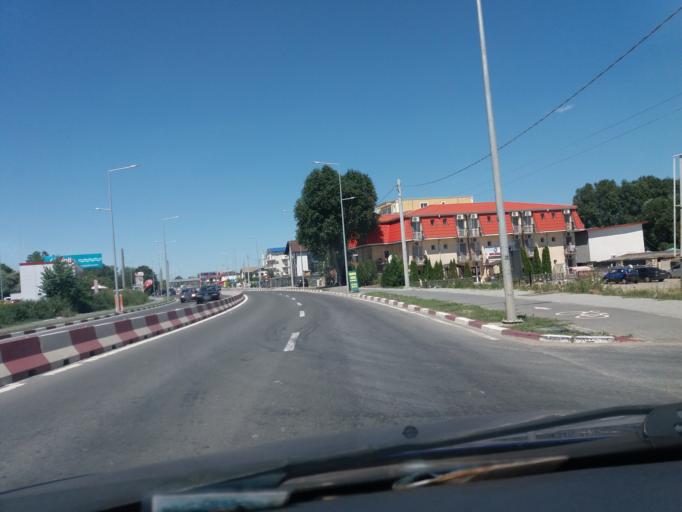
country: RO
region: Constanta
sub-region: Comuna Navodari
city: Navodari
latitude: 44.3102
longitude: 28.6247
